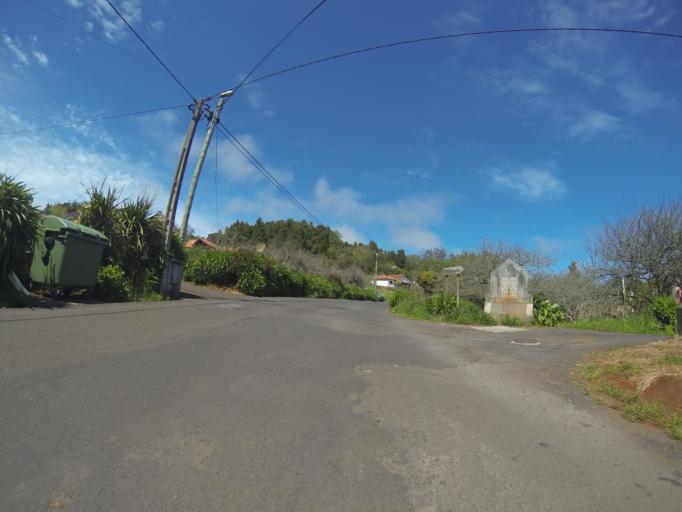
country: PT
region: Madeira
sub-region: Santa Cruz
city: Santa Cruz
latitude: 32.7254
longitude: -16.8223
